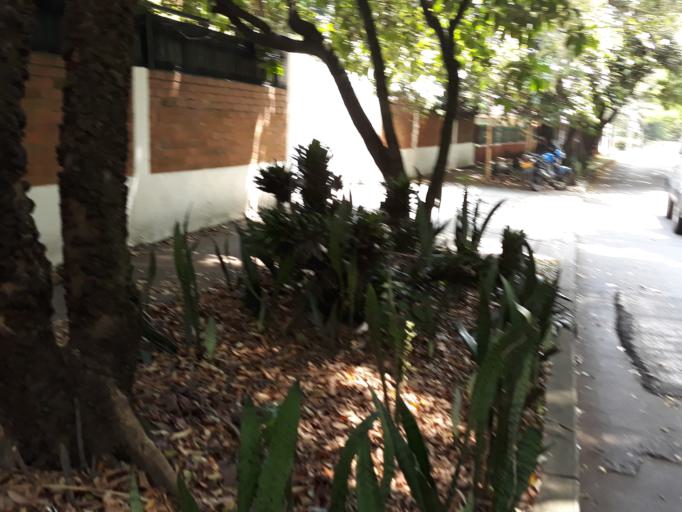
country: CO
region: Valle del Cauca
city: Cali
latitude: 3.3820
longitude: -76.5403
